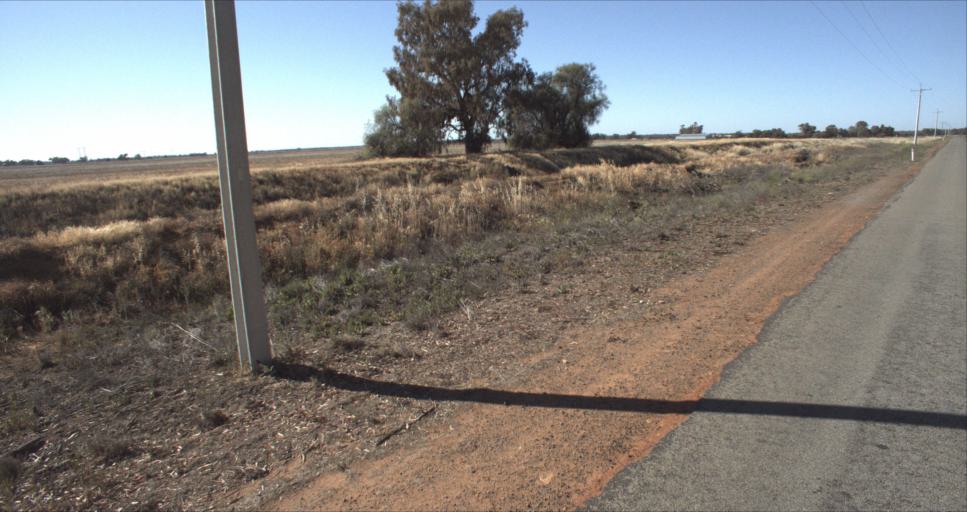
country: AU
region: New South Wales
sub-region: Leeton
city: Leeton
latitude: -34.5766
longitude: 146.3096
